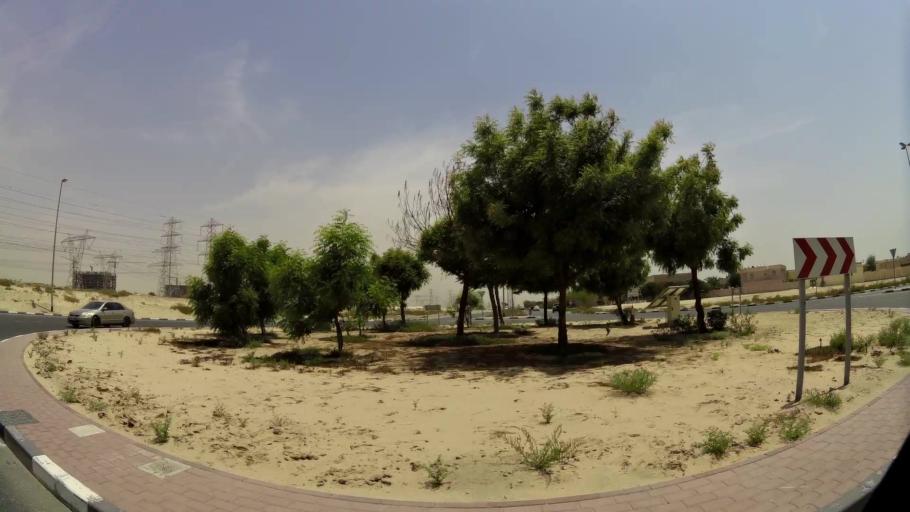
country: AE
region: Ash Shariqah
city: Sharjah
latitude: 25.1999
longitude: 55.3921
